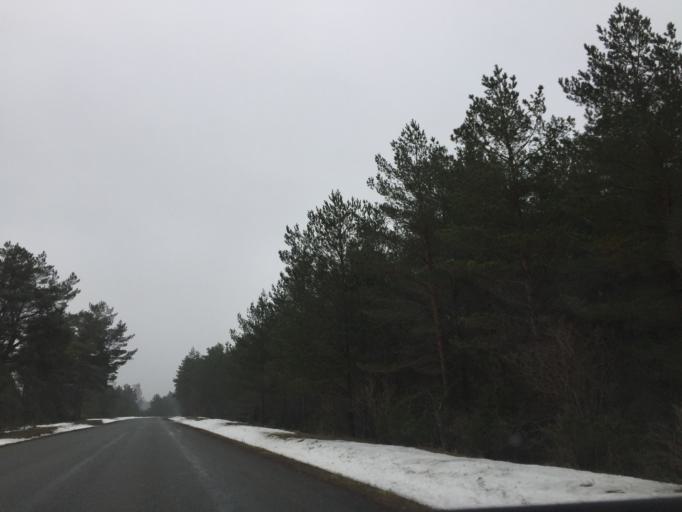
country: EE
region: Saare
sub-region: Orissaare vald
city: Orissaare
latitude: 58.4133
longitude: 22.8158
